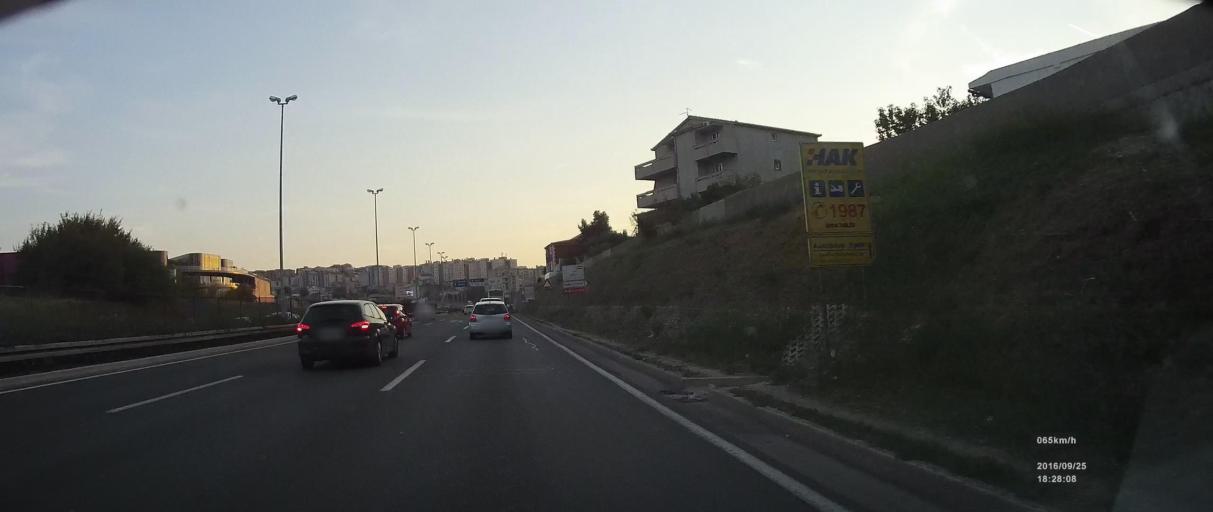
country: HR
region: Splitsko-Dalmatinska
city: Vranjic
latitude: 43.5222
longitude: 16.4850
